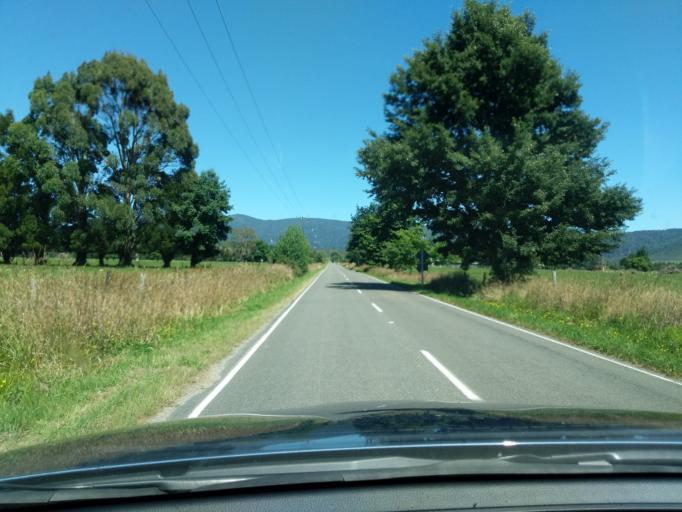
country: NZ
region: Tasman
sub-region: Tasman District
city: Takaka
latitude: -40.7290
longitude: 172.6357
